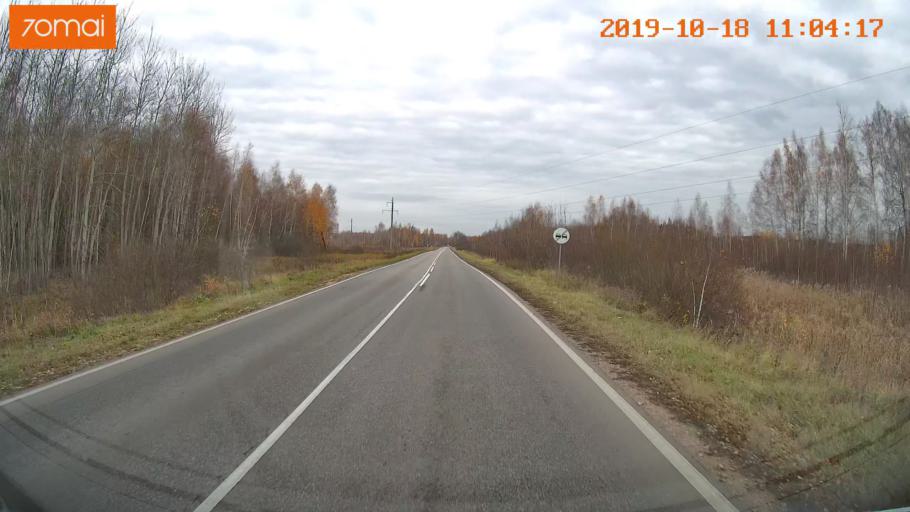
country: RU
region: Tula
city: Yepifan'
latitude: 53.8920
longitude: 38.5500
